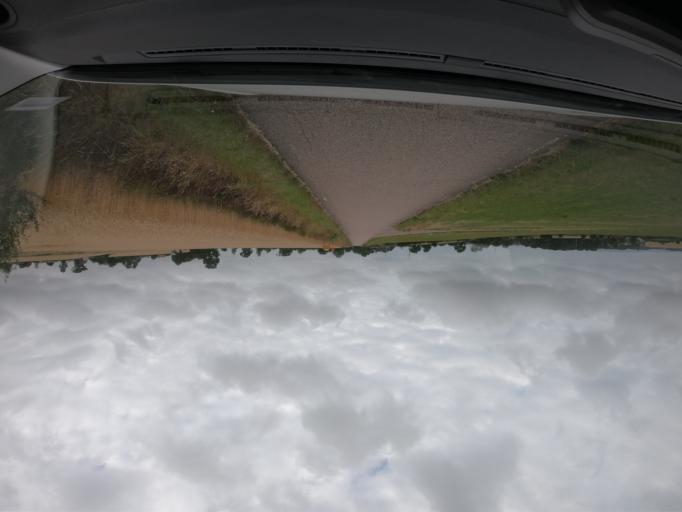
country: SE
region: Skane
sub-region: Bastads Kommun
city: Forslov
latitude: 56.3434
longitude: 12.8134
